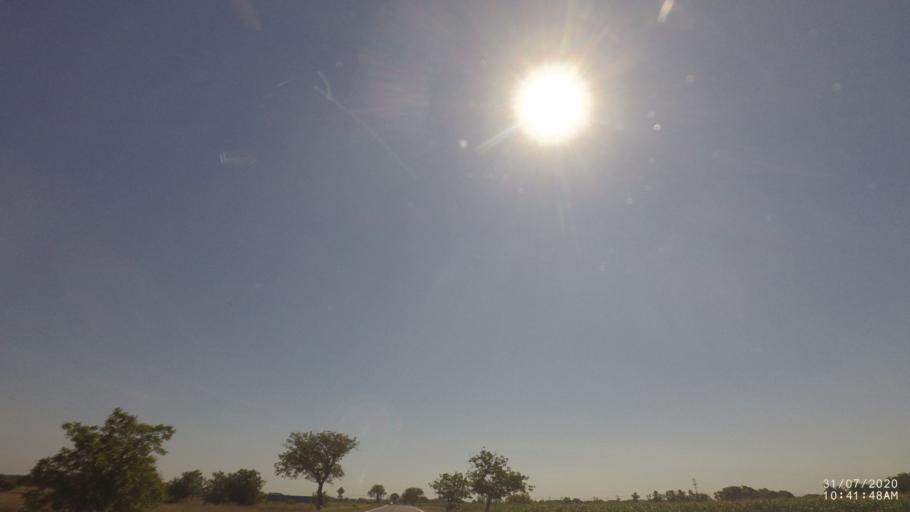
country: SK
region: Trnavsky
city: Dunajska Streda
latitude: 47.9997
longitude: 17.4938
